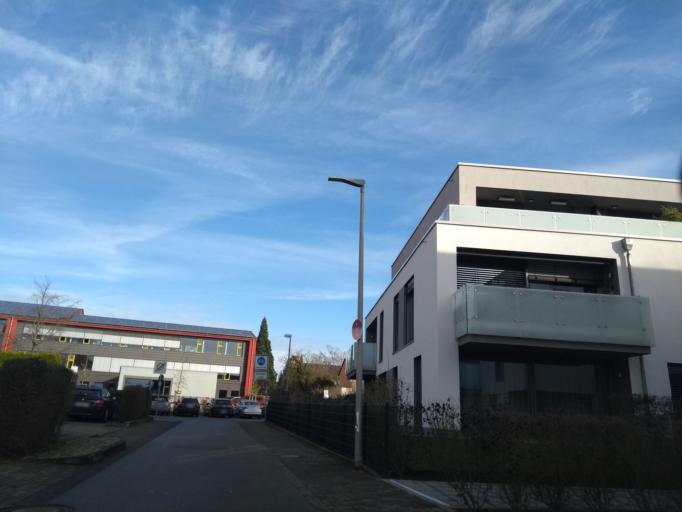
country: DE
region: North Rhine-Westphalia
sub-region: Regierungsbezirk Detmold
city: Lemgo
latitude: 52.0313
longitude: 8.8970
